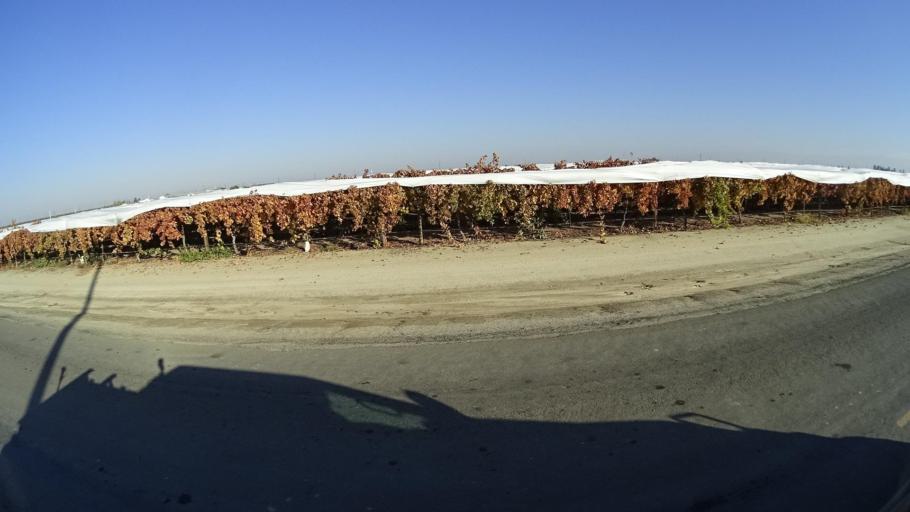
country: US
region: California
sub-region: Kern County
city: Delano
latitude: 35.7686
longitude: -119.1972
